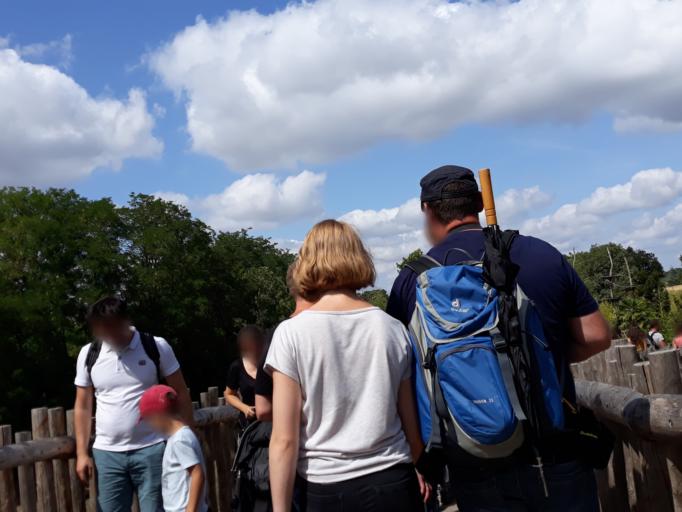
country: FR
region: Centre
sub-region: Departement du Loir-et-Cher
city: Saint-Aignan
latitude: 47.2429
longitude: 1.3493
